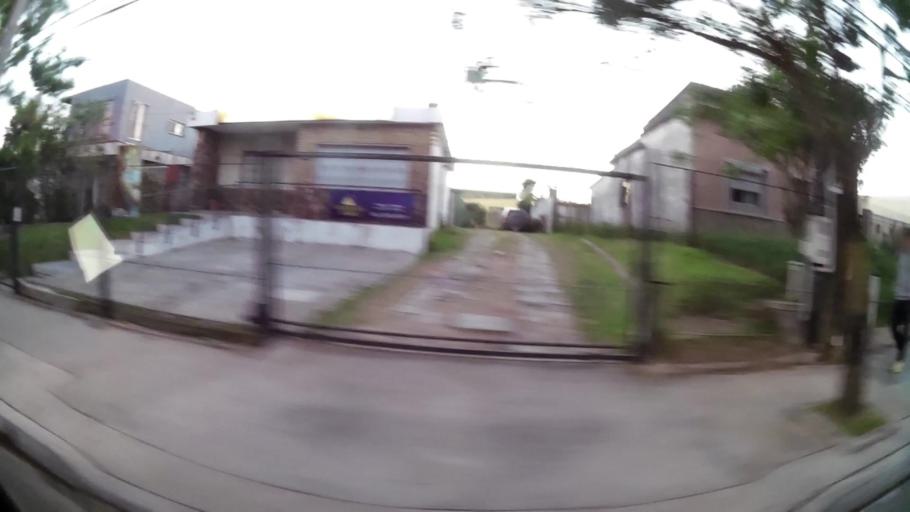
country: UY
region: Canelones
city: Paso de Carrasco
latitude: -34.8762
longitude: -56.1026
